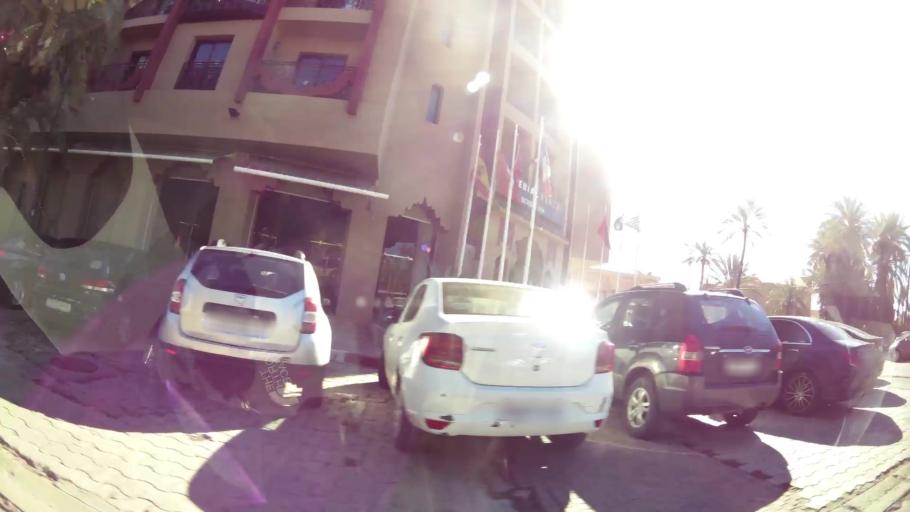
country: MA
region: Marrakech-Tensift-Al Haouz
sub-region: Marrakech
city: Marrakesh
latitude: 31.6458
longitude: -8.0170
